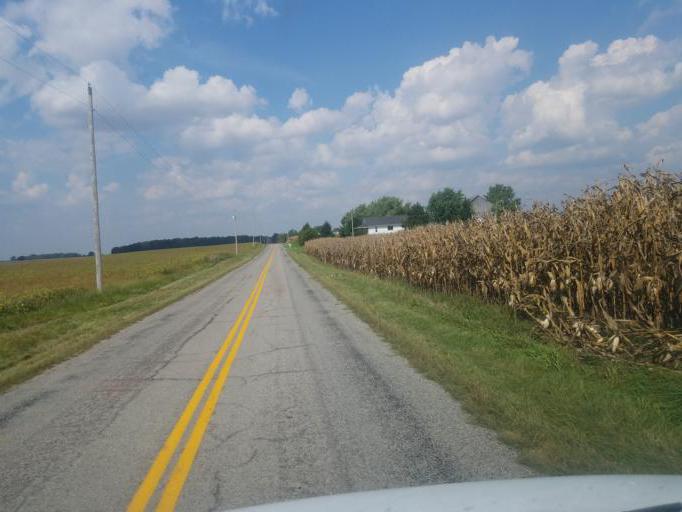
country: US
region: Ohio
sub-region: Hardin County
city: Ada
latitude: 40.6389
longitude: -83.8838
